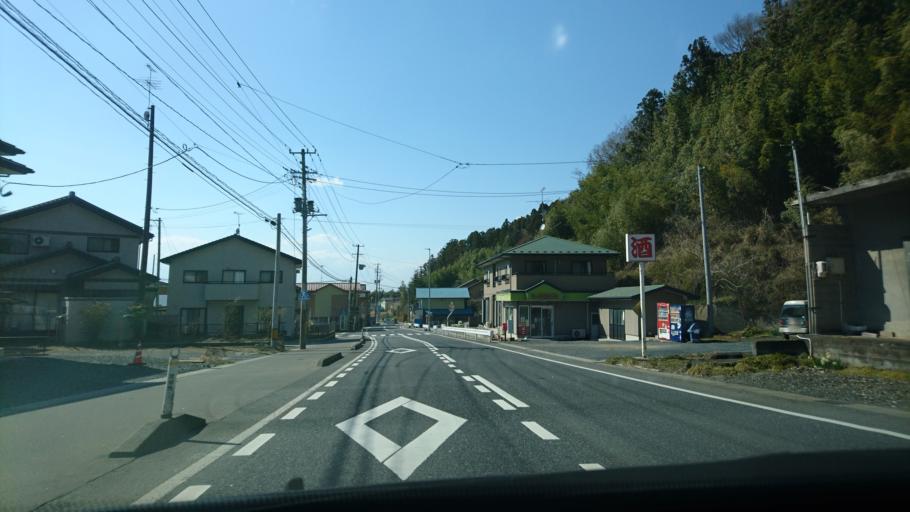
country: JP
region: Miyagi
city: Wakuya
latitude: 38.7043
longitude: 141.2816
